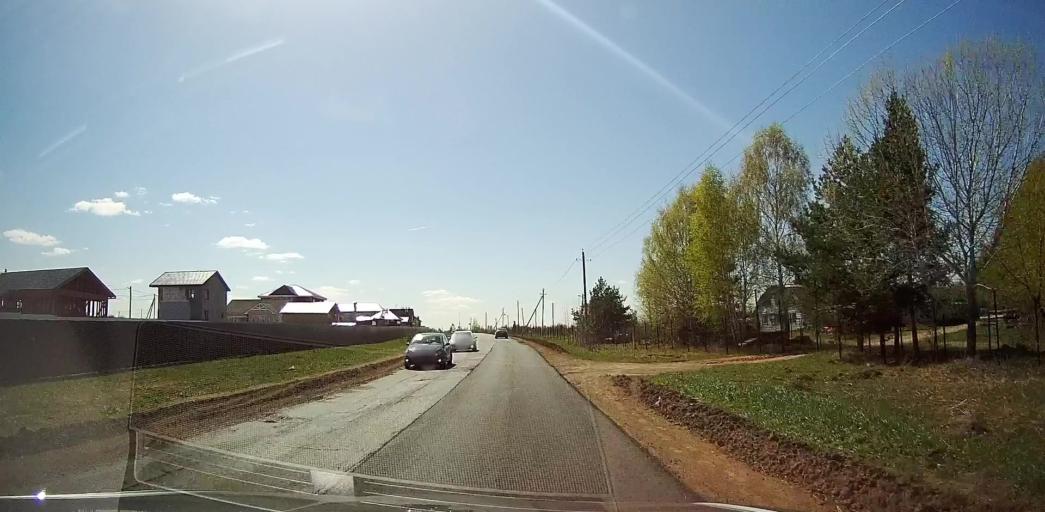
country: RU
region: Moskovskaya
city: Malyshevo
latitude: 55.4679
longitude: 38.3866
